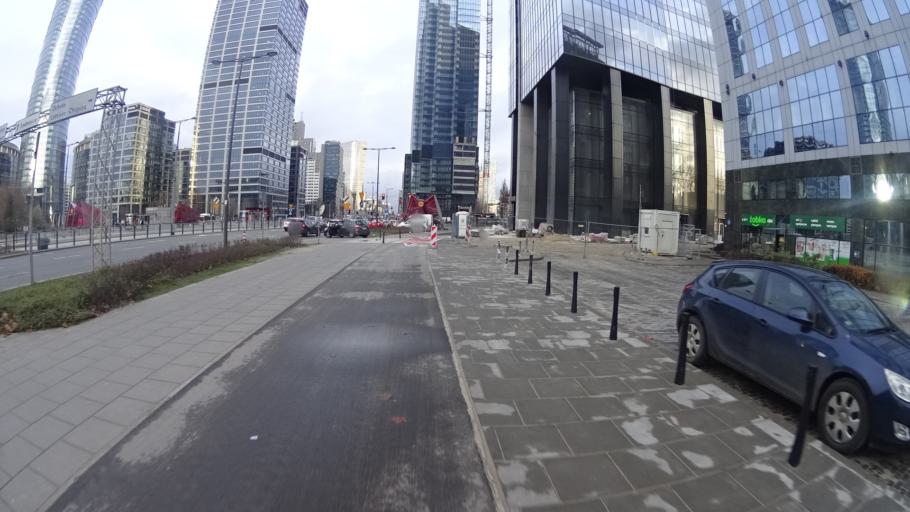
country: PL
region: Masovian Voivodeship
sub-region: Warszawa
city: Ochota
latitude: 52.2296
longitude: 20.9824
